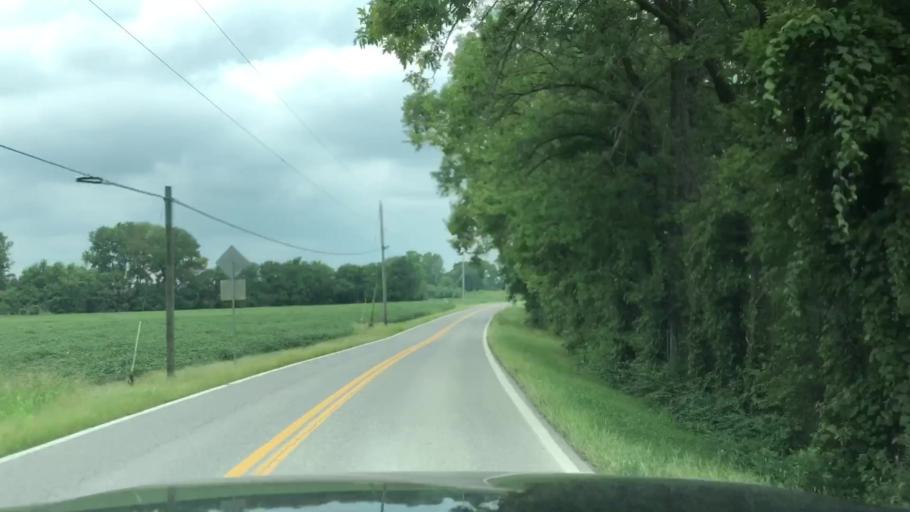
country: US
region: Missouri
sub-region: Saint Louis County
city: Bridgeton
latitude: 38.7972
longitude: -90.4206
